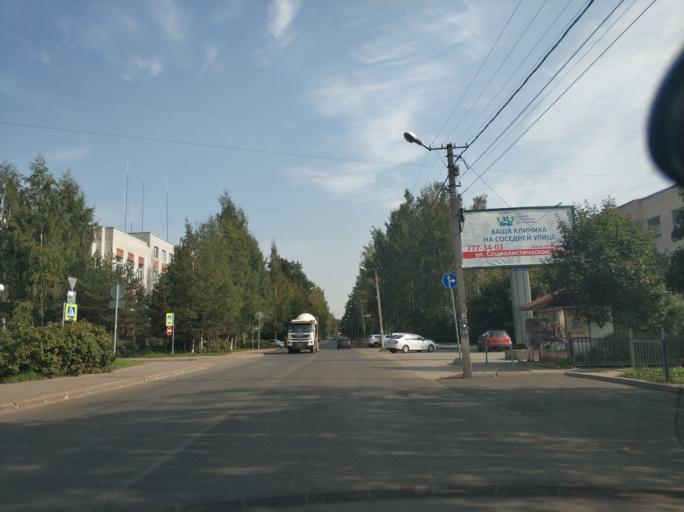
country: RU
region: Leningrad
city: Vsevolozhsk
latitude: 60.0192
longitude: 30.6475
